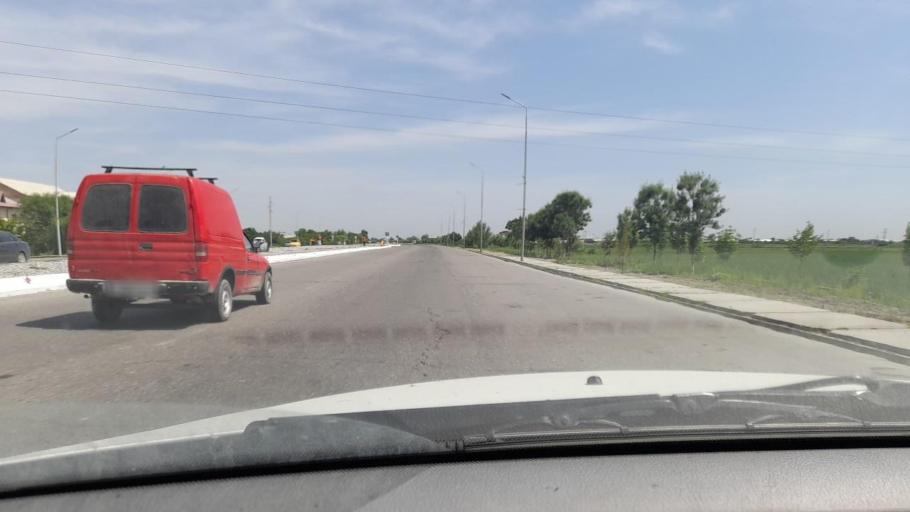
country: UZ
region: Bukhara
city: Galaosiyo
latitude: 39.8672
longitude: 64.4512
